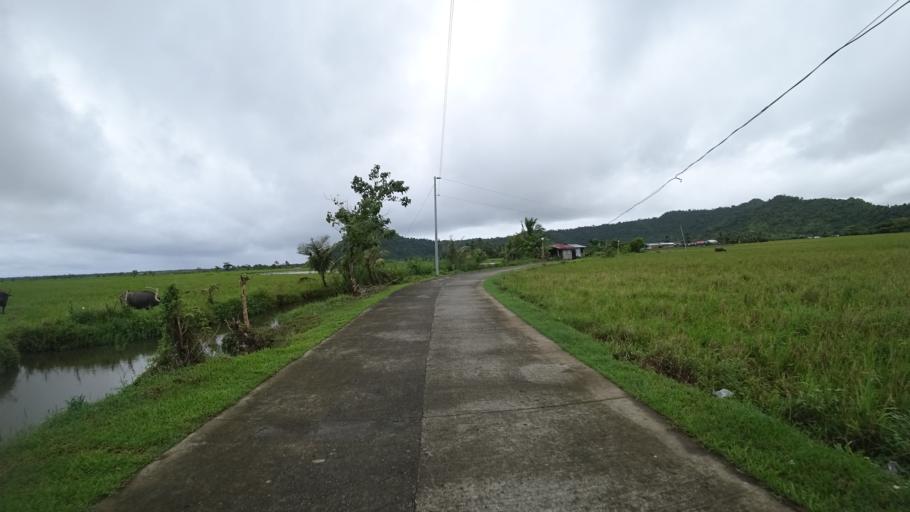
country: PH
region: Eastern Visayas
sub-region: Province of Leyte
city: Bugho
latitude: 10.7946
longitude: 124.9729
